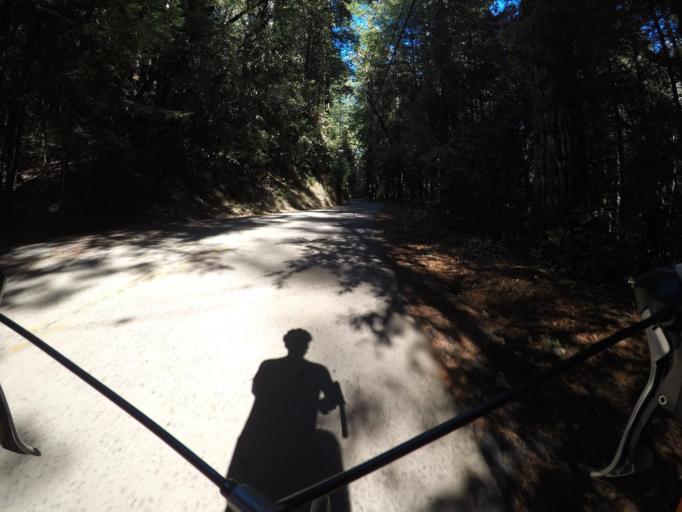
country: US
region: California
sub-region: Santa Clara County
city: Lexington Hills
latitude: 37.1215
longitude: -121.9860
